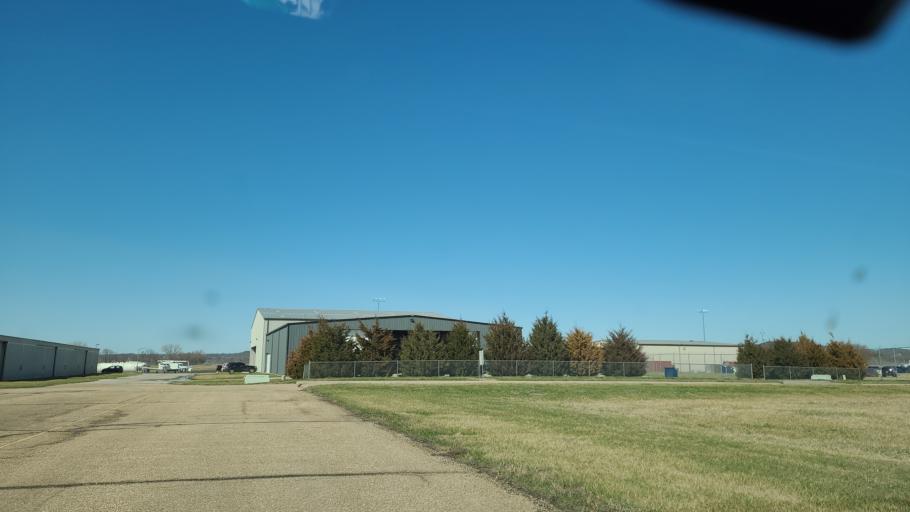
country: US
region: Kansas
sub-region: Douglas County
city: Lawrence
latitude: 39.0039
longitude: -95.2178
